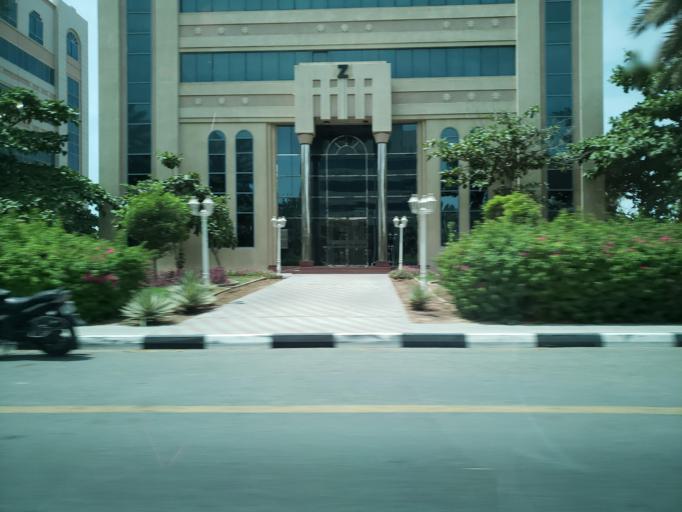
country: AE
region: Ash Shariqah
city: Sharjah
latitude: 25.3282
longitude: 55.4970
